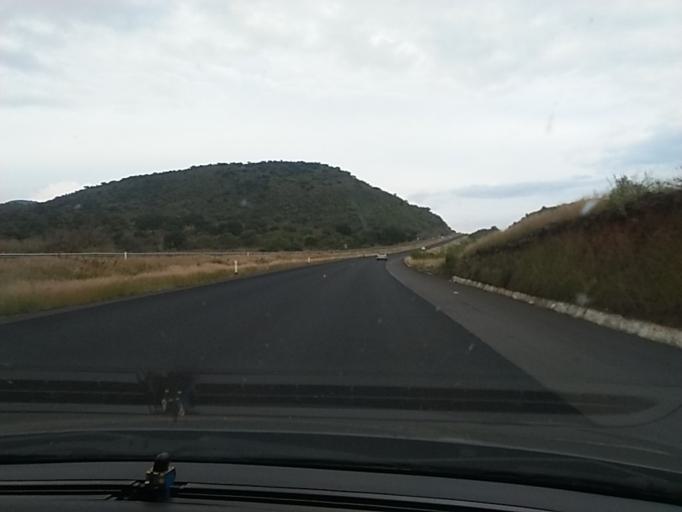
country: MX
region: Mexico
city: Huaniqueo de Morales
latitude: 19.8870
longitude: -101.4601
